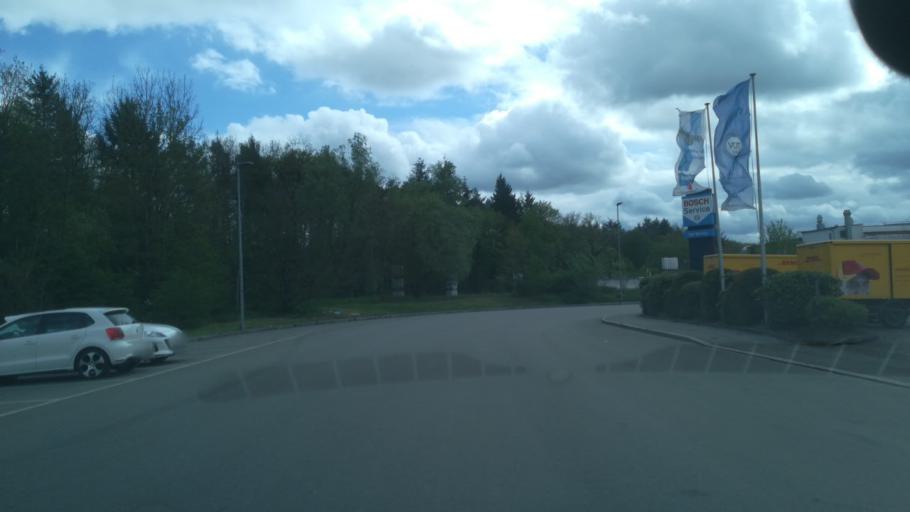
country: DE
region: Baden-Wuerttemberg
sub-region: Freiburg Region
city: Moos
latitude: 47.7538
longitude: 8.8896
